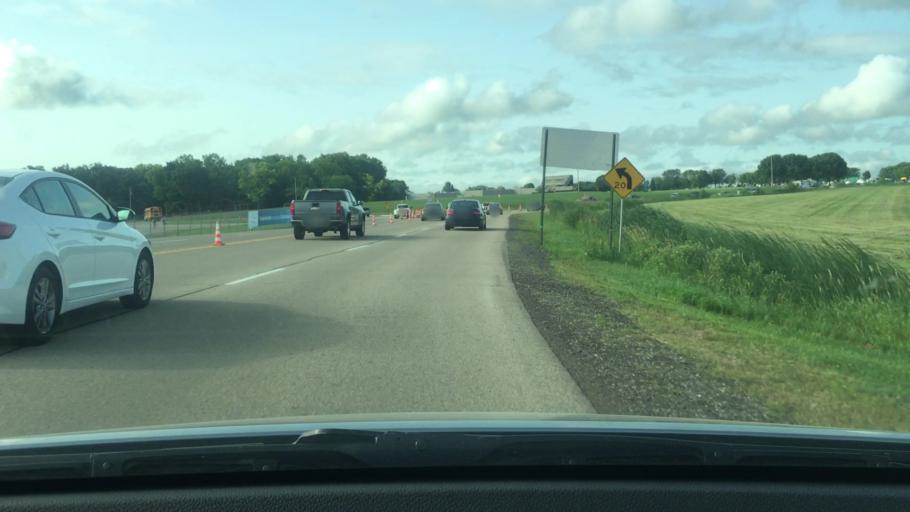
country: US
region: Wisconsin
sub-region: Winnebago County
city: Oshkosh
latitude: 43.9913
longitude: -88.5778
